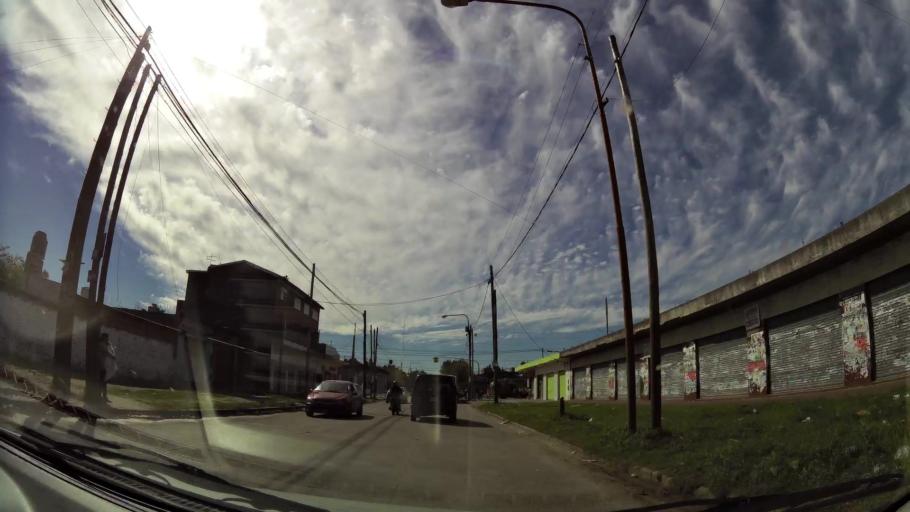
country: AR
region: Buenos Aires
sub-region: Partido de Almirante Brown
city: Adrogue
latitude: -34.7693
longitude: -58.3157
